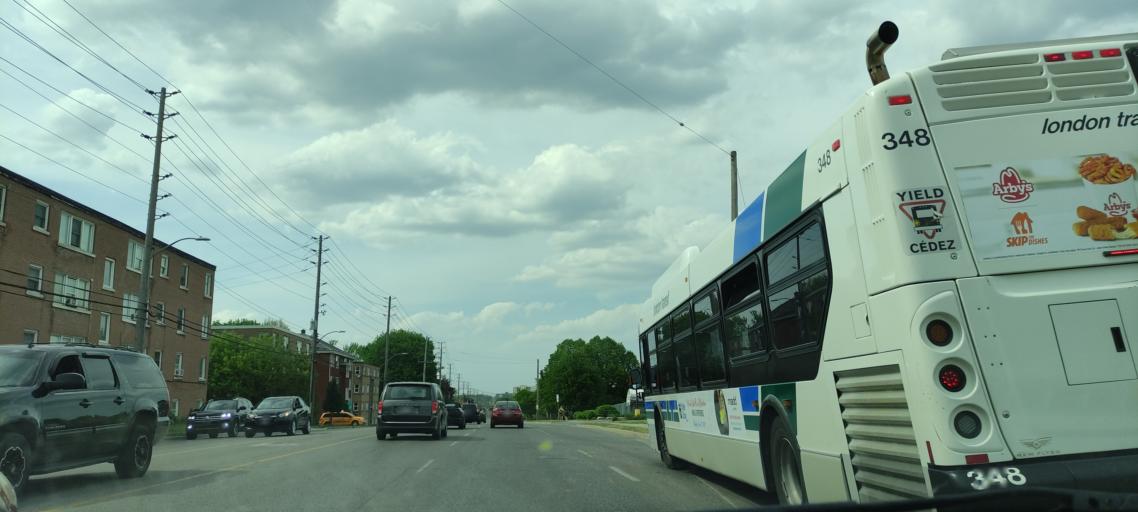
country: CA
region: Ontario
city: London
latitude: 43.0061
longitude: -81.2402
